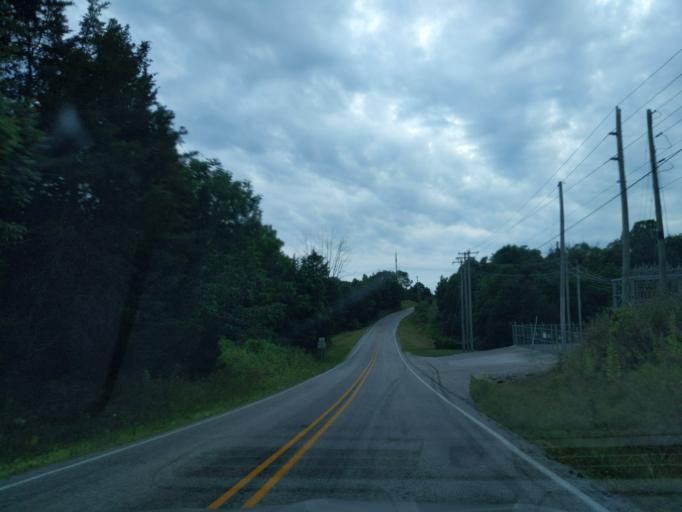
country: US
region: Indiana
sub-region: Ripley County
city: Osgood
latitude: 39.1935
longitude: -85.2118
